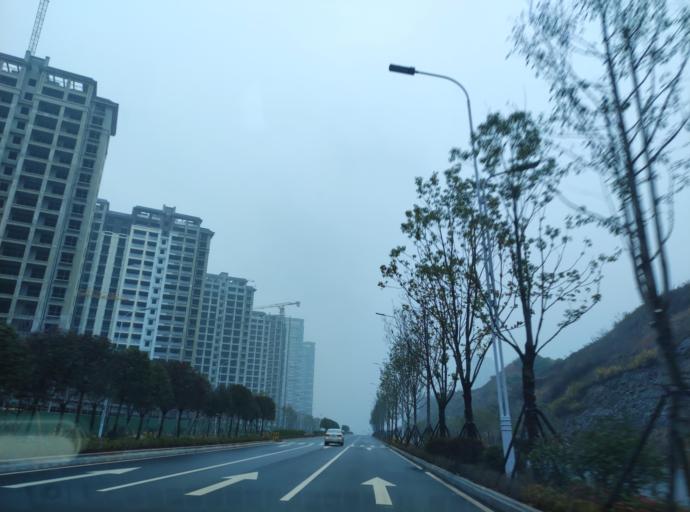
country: CN
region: Jiangxi Sheng
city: Pingxiang
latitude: 27.6648
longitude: 113.8426
